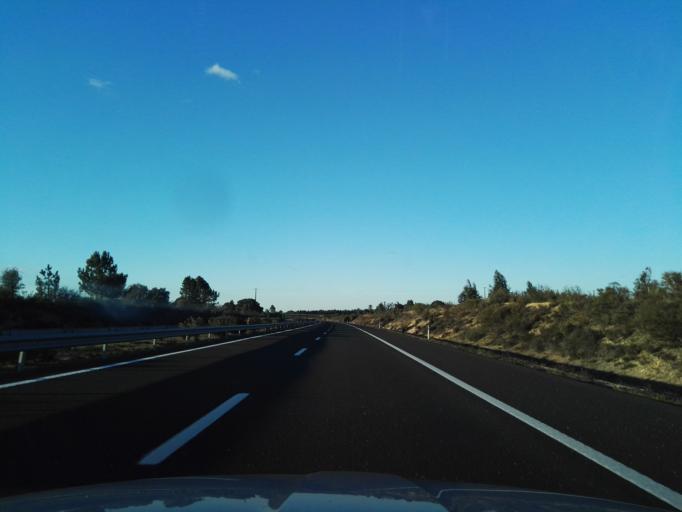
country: PT
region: Santarem
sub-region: Benavente
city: Poceirao
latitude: 38.7809
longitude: -8.6847
